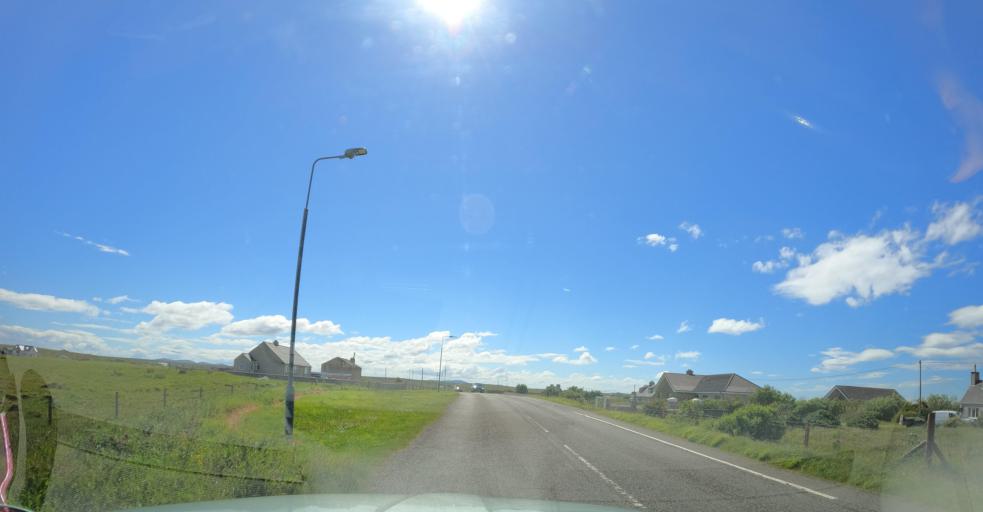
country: GB
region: Scotland
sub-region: Eilean Siar
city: Isle of Lewis
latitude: 58.4011
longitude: -6.4671
